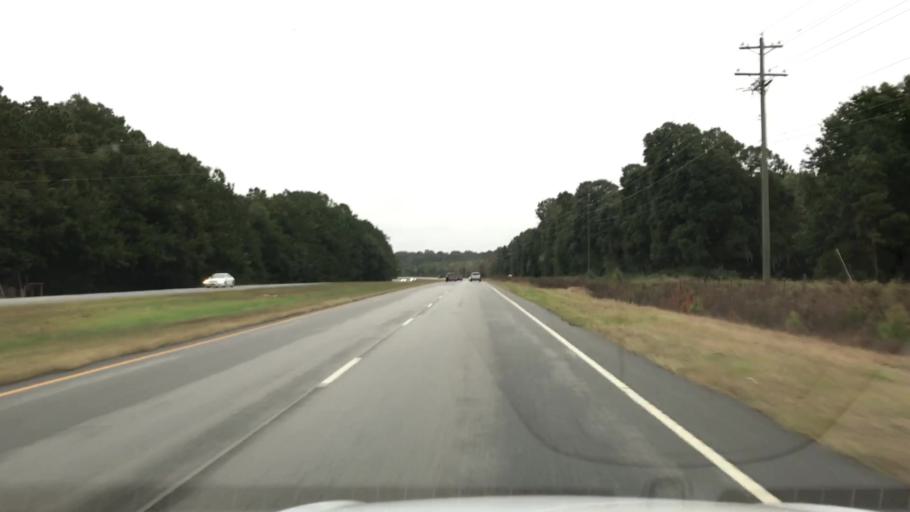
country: US
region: South Carolina
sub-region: Charleston County
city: Isle of Palms
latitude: 32.9151
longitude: -79.7191
